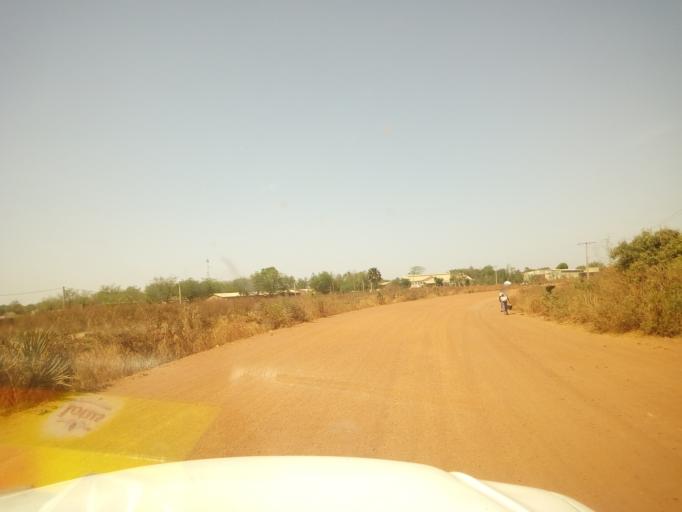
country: ML
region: Bamako
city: Bamako
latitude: 12.6197
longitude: -7.7737
